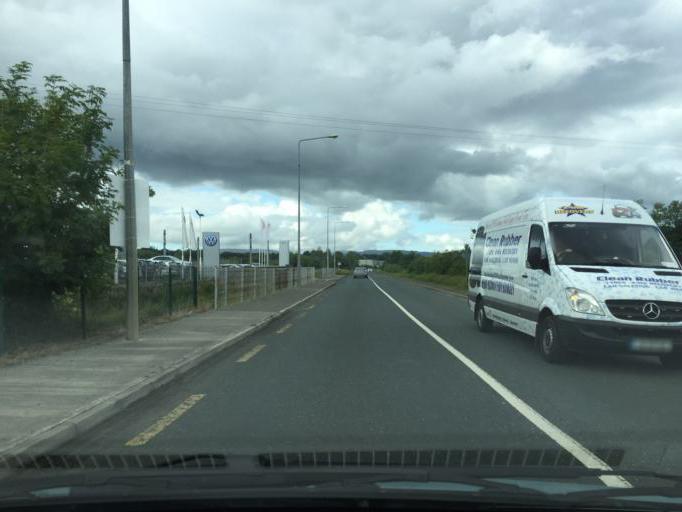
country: IE
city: Ballisodare
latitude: 54.2227
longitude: -8.4981
